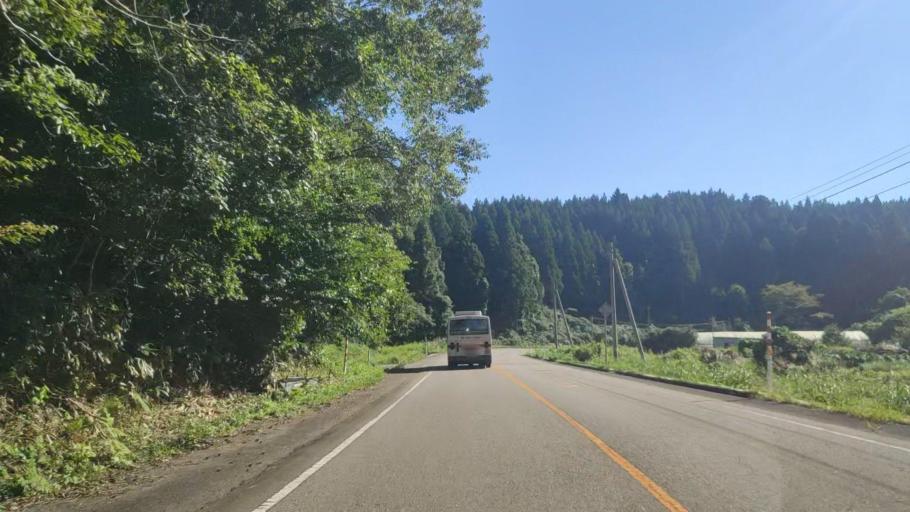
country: JP
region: Ishikawa
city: Nanao
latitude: 37.2430
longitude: 136.9880
